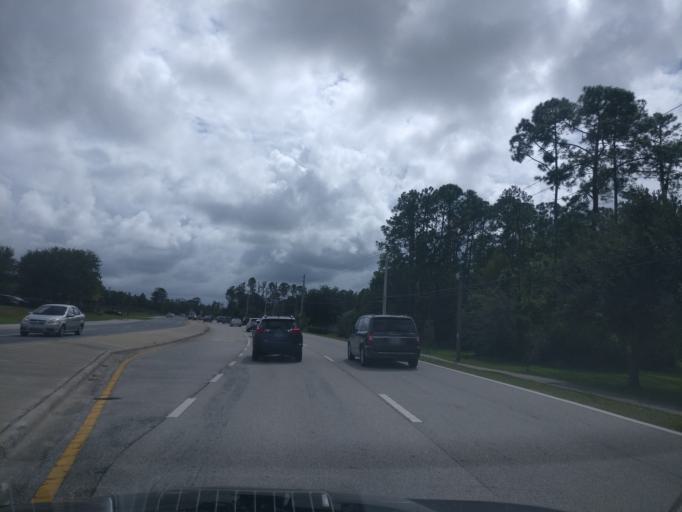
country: US
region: Florida
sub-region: Flagler County
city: Bunnell
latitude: 29.4876
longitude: -81.2219
